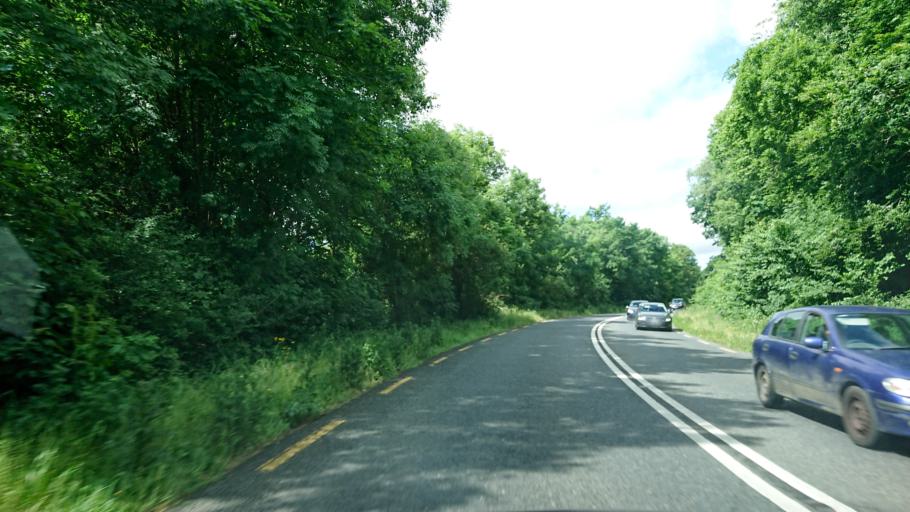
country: IE
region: Leinster
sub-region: Kilkenny
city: Mooncoin
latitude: 52.2315
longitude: -7.2181
